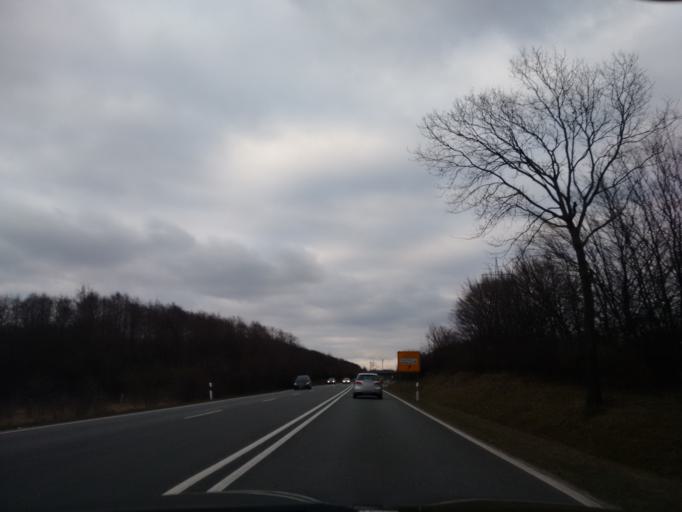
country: DE
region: North Rhine-Westphalia
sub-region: Regierungsbezirk Detmold
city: Paderborn
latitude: 51.7130
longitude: 8.8121
